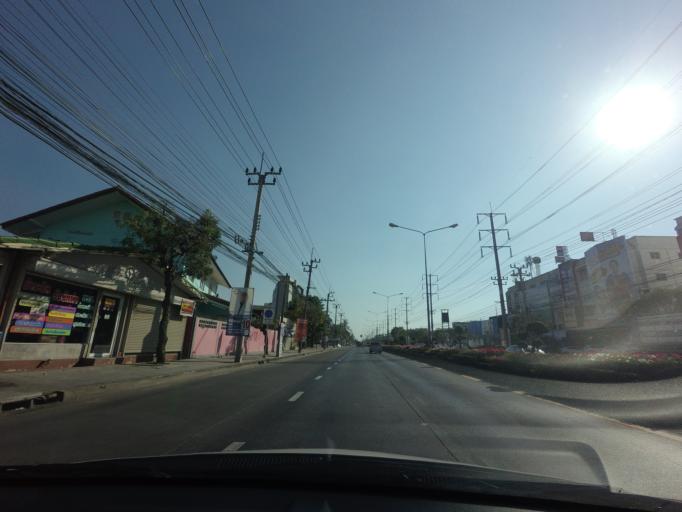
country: TH
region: Bangkok
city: Nong Chok
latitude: 13.8501
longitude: 100.8601
